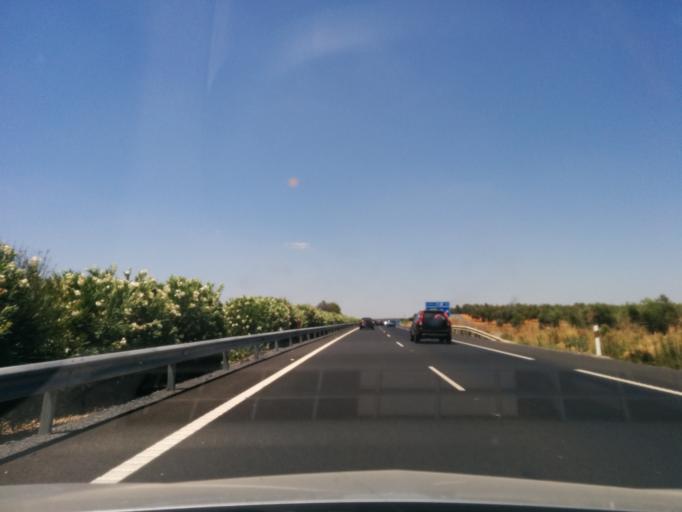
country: ES
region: Andalusia
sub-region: Provincia de Huelva
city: Chucena
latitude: 37.3537
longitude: -6.3730
